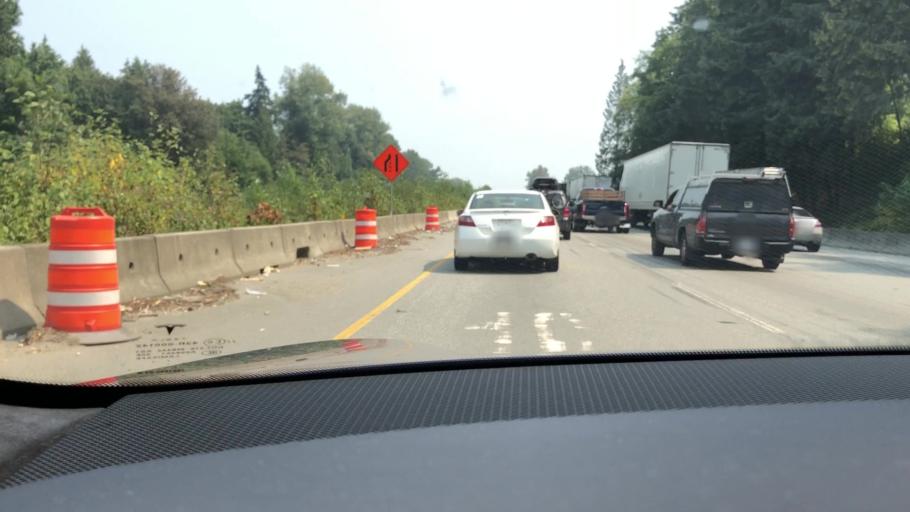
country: CA
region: British Columbia
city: Walnut Grove
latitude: 49.1598
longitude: -122.6556
